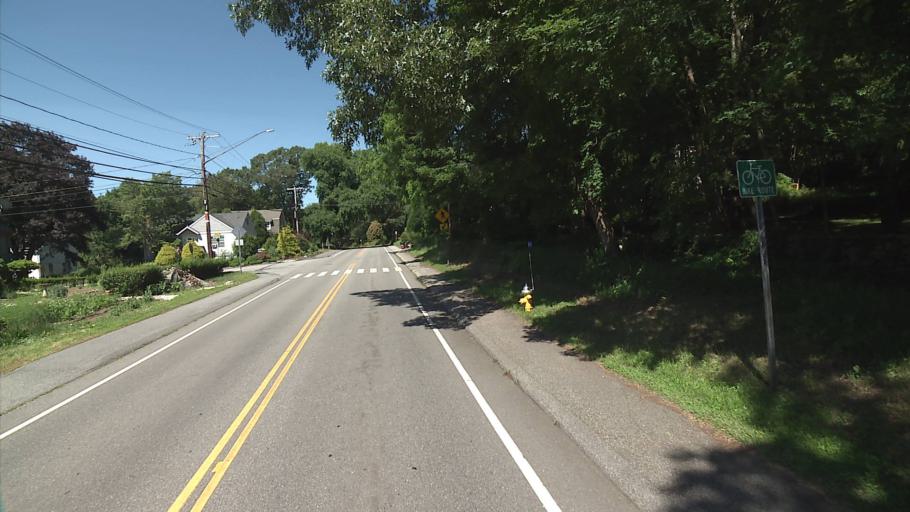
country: US
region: Connecticut
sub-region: New London County
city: Noank
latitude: 41.3409
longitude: -71.9854
